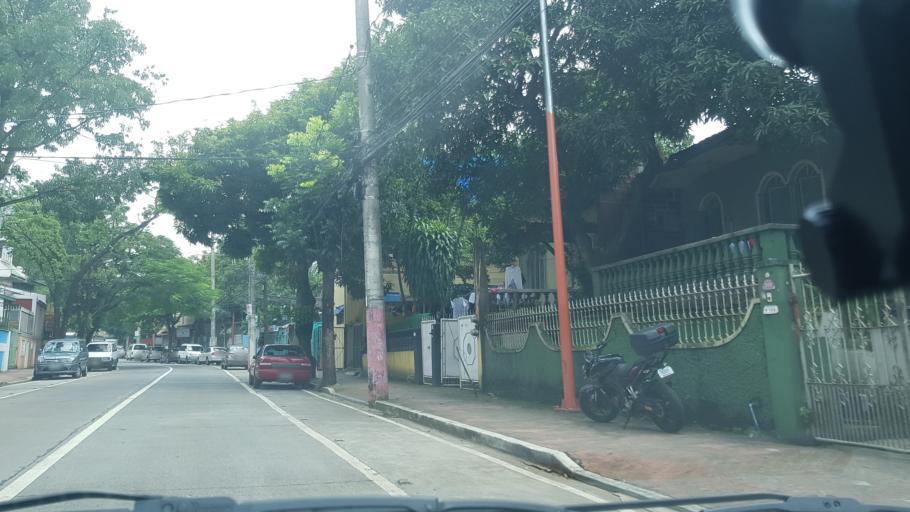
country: PH
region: Calabarzon
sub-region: Province of Rizal
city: Antipolo
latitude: 14.6572
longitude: 121.1185
